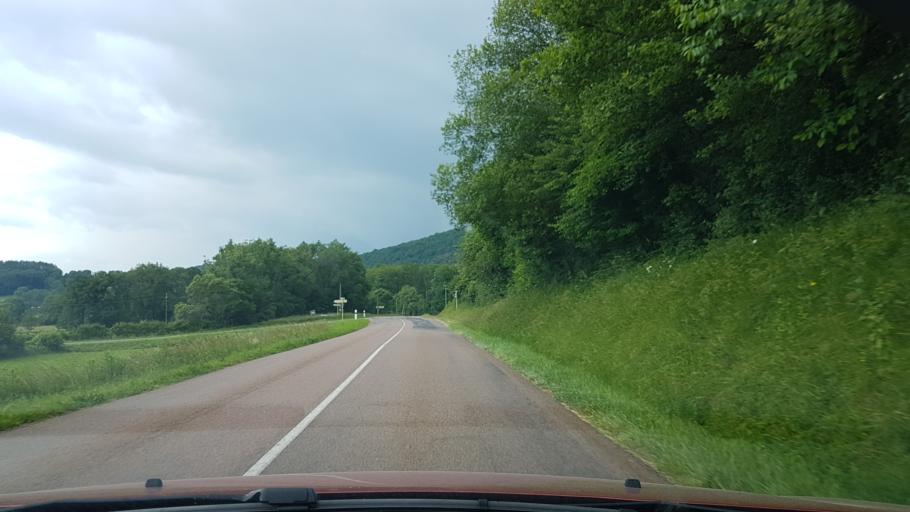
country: FR
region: Franche-Comte
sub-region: Departement du Jura
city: Orgelet
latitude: 46.5605
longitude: 5.6666
